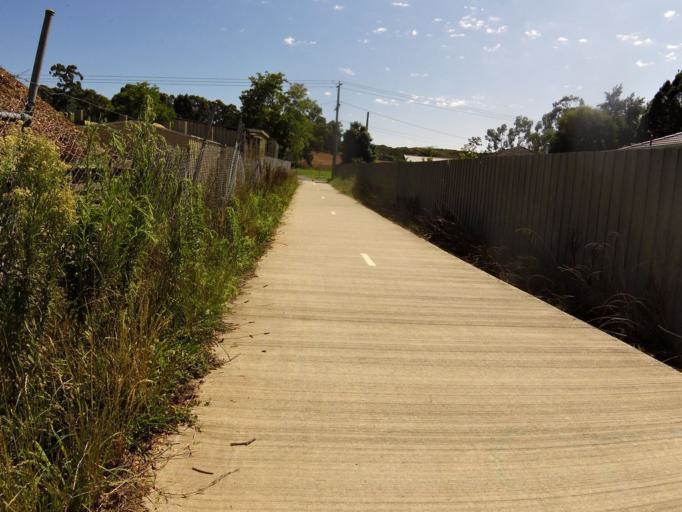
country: AU
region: Victoria
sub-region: Yarra Ranges
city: Kilsyth
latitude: -37.7758
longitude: 145.3329
